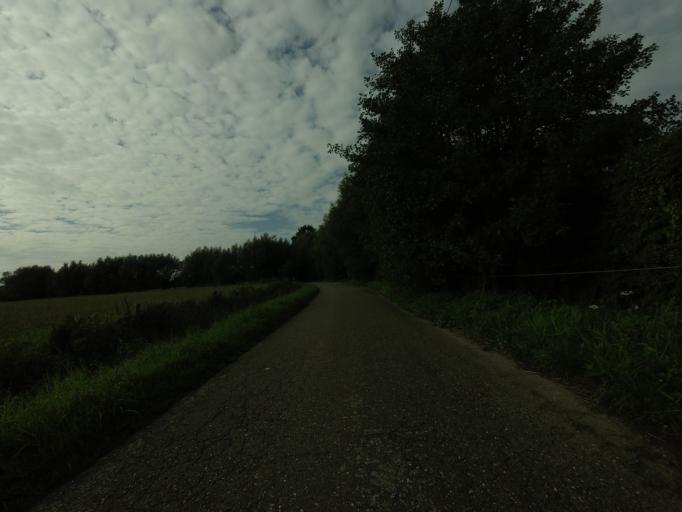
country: BE
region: Flanders
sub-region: Provincie Vlaams-Brabant
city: Kapelle-op-den-Bos
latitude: 51.0291
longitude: 4.3315
